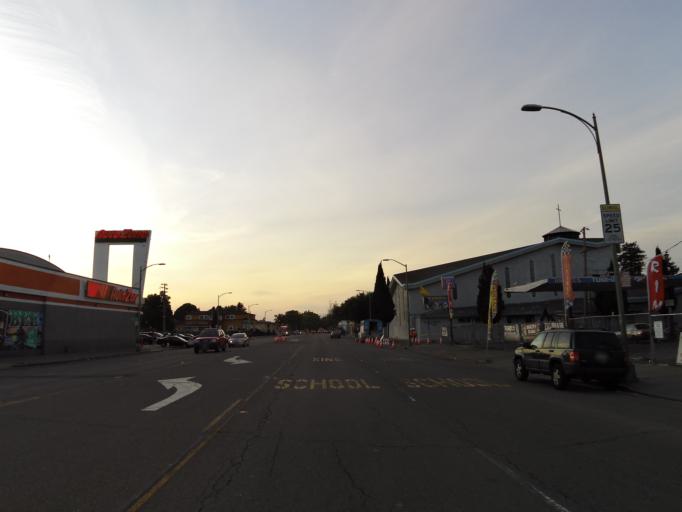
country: US
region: California
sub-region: Alameda County
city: San Leandro
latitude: 37.7416
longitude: -122.1685
